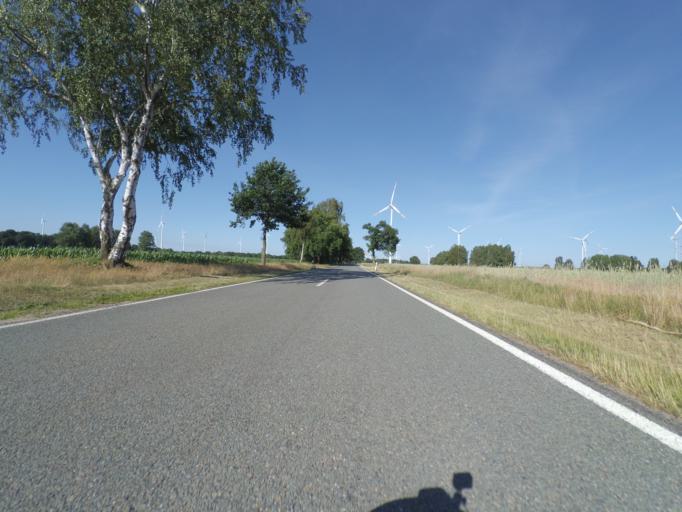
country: DE
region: Brandenburg
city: Putlitz
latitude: 53.3350
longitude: 12.0468
